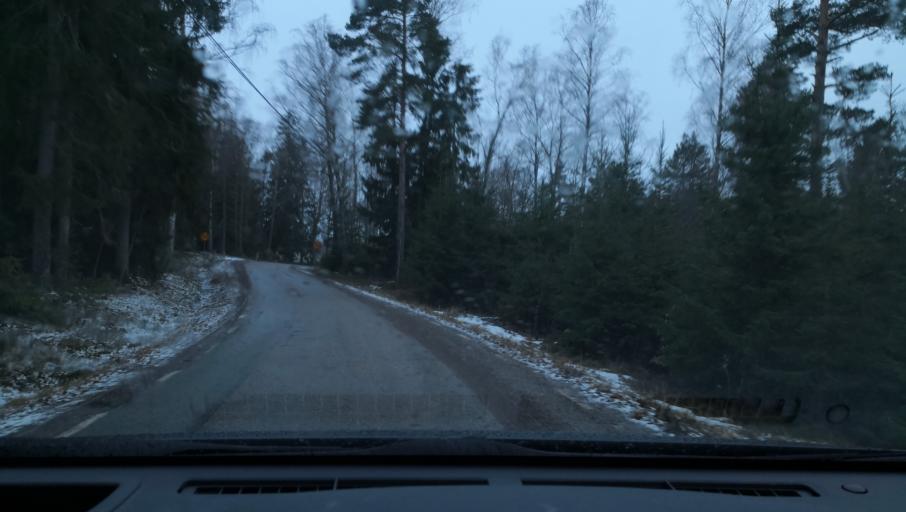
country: SE
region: Soedermanland
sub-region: Eskilstuna Kommun
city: Arla
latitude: 59.4496
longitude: 16.7860
